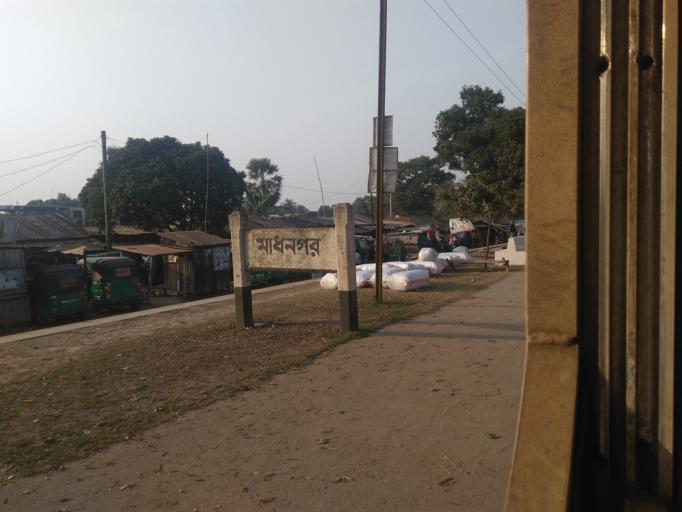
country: BD
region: Rajshahi
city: Par Naogaon
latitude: 24.5342
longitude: 88.9618
